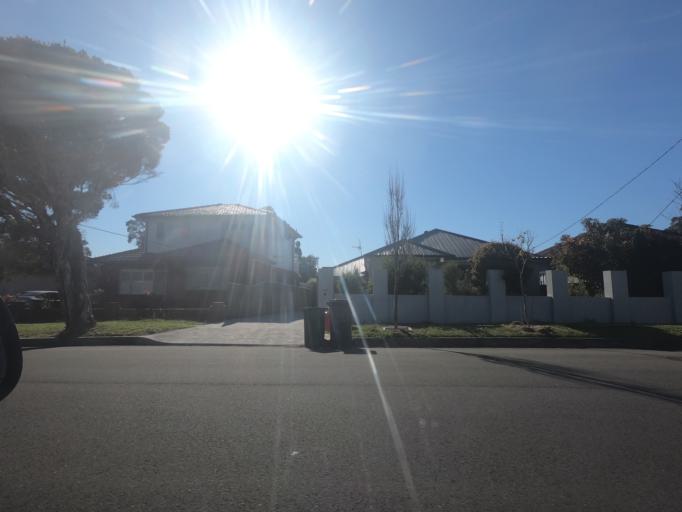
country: AU
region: New South Wales
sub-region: Wollongong
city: Fairy Meadow
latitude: -34.3876
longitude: 150.8894
